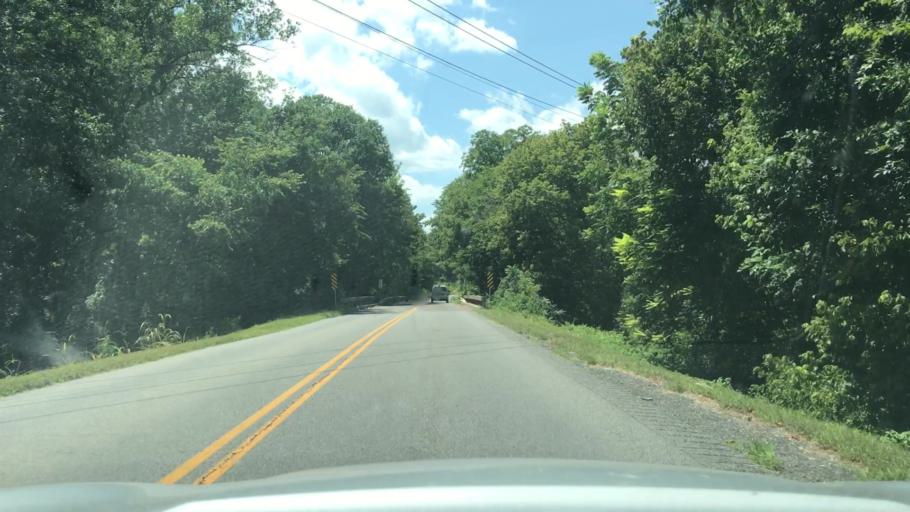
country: US
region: Kentucky
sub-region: Christian County
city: Hopkinsville
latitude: 36.8892
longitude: -87.4567
